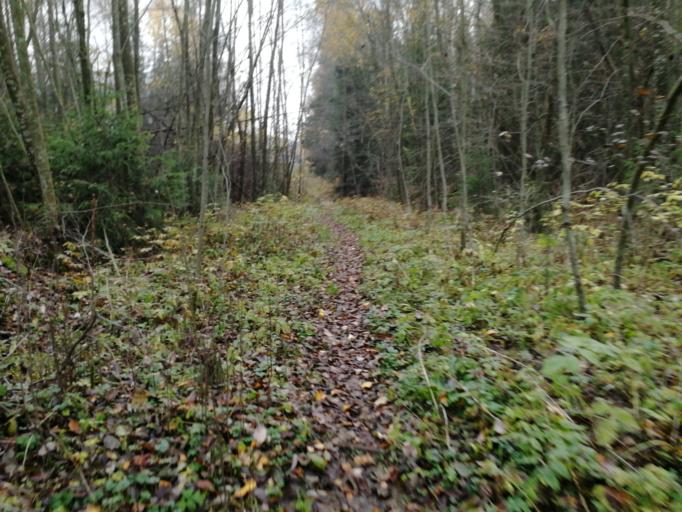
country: FI
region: Pirkanmaa
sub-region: Tampere
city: Tampere
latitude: 61.4479
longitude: 23.8929
